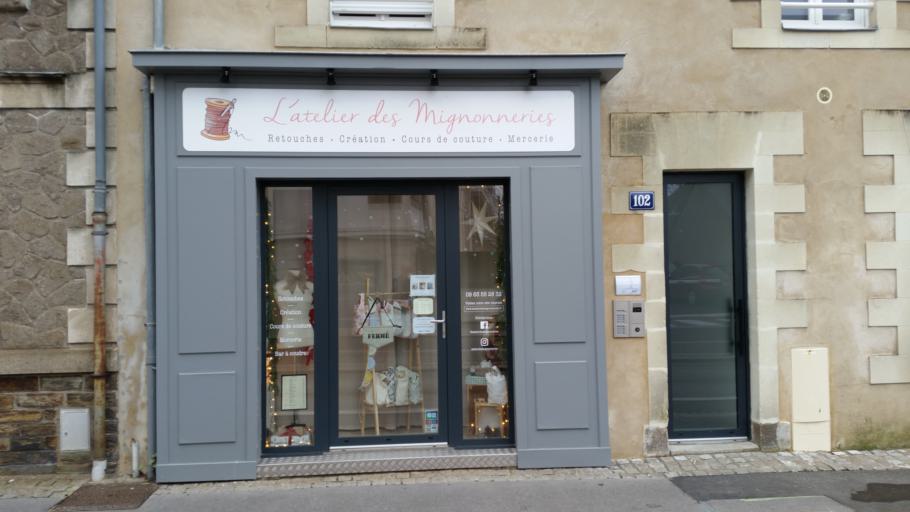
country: FR
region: Pays de la Loire
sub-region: Departement de la Loire-Atlantique
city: Nantes
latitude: 47.2279
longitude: -1.5705
